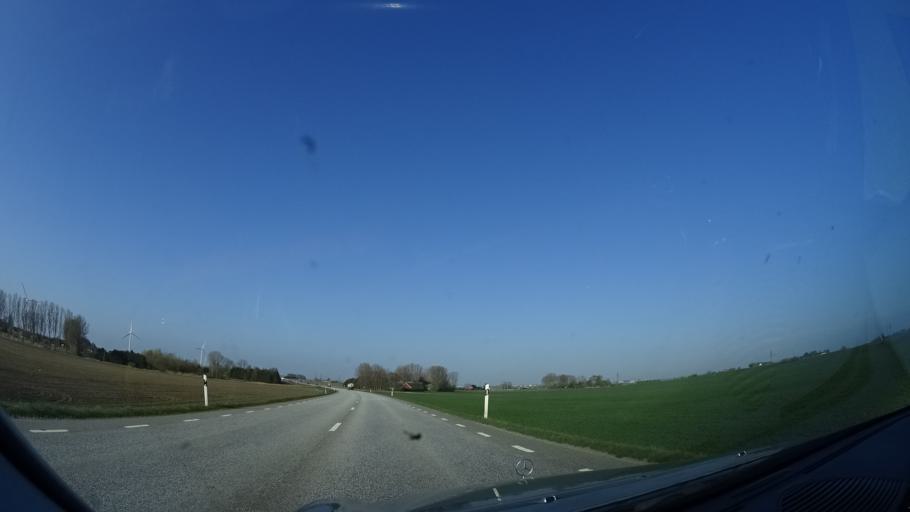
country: SE
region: Skane
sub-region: Landskrona
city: Asmundtorp
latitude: 55.8880
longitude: 12.9155
